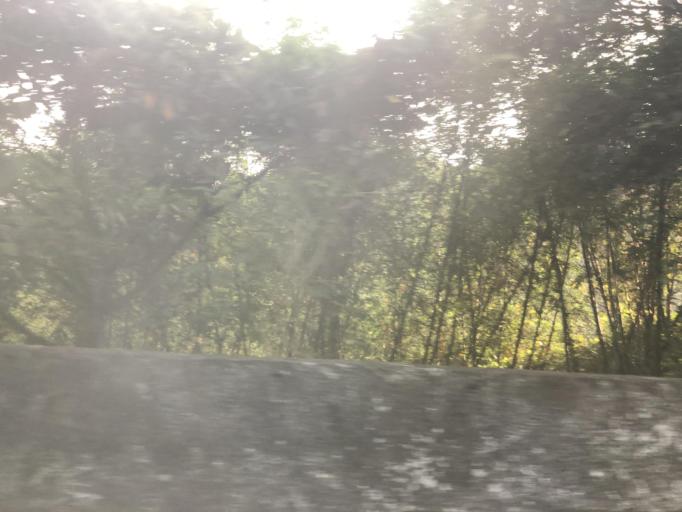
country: TW
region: Taiwan
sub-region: Keelung
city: Keelung
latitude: 25.1754
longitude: 121.6526
